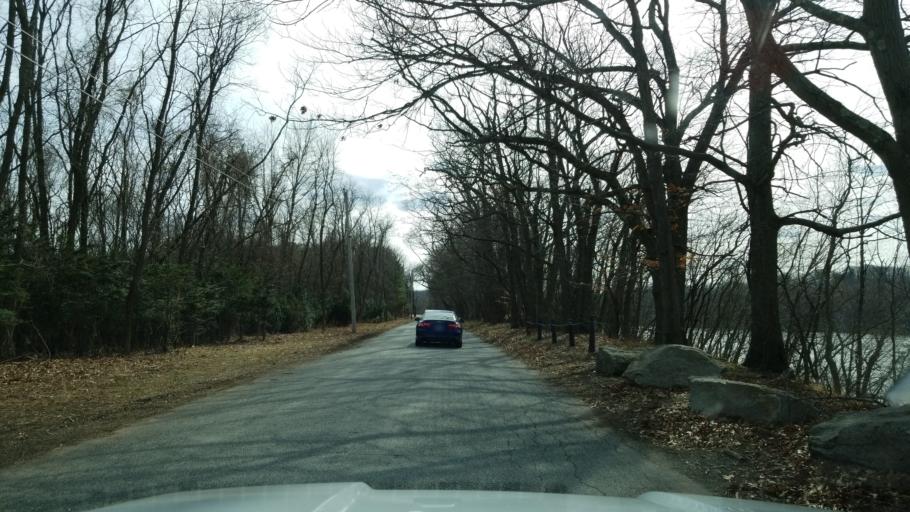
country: US
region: Connecticut
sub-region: Middlesex County
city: Cromwell
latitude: 41.6400
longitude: -72.6255
